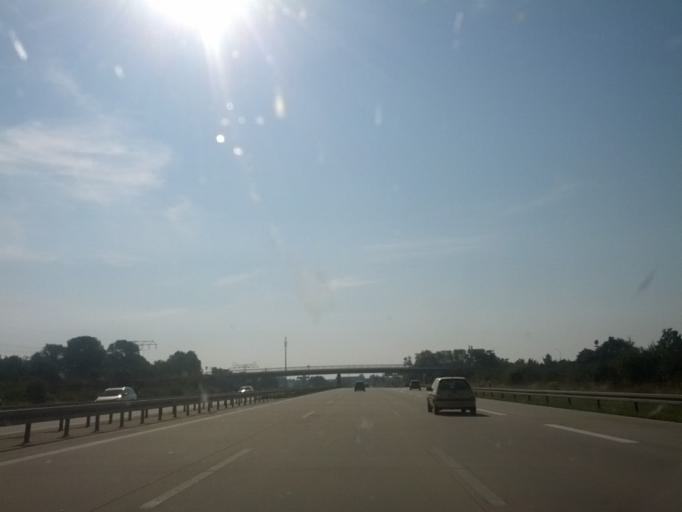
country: DE
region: Brandenburg
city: Petershagen
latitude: 52.5035
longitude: 13.7428
